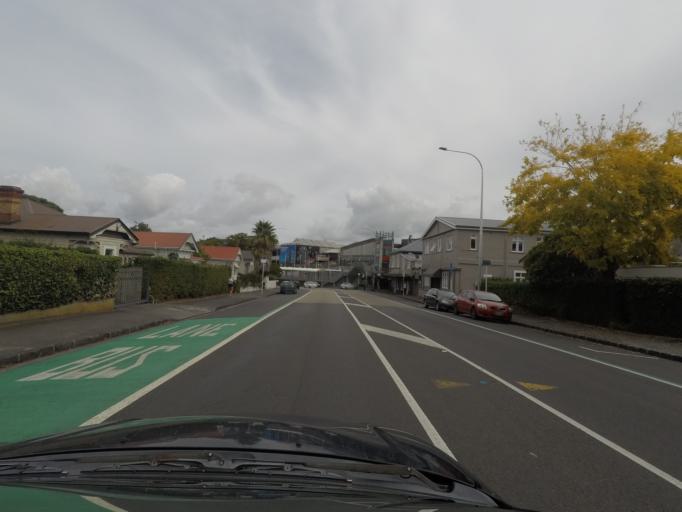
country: NZ
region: Auckland
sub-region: Auckland
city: Auckland
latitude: -36.8729
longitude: 174.7454
